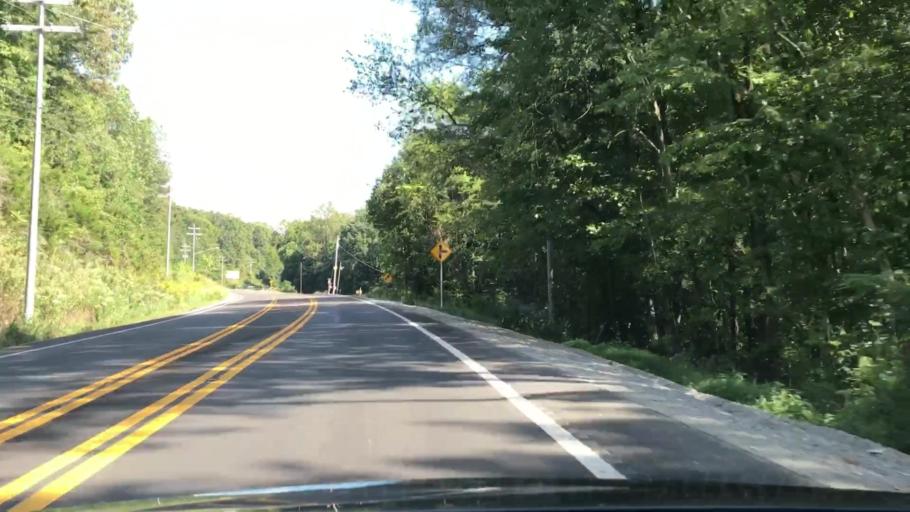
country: US
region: Alabama
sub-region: Limestone County
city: Ardmore
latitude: 35.0054
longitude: -86.8730
